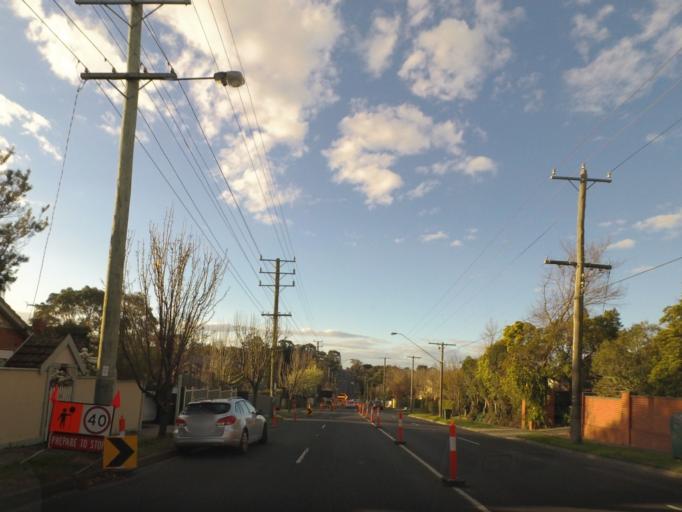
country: AU
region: Victoria
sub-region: Whitehorse
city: Surrey Hills
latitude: -37.8326
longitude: 145.0988
